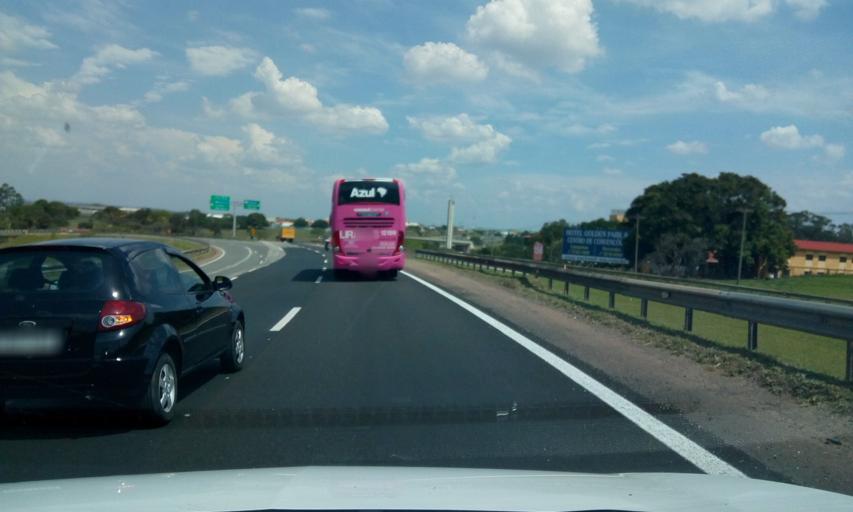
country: BR
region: Sao Paulo
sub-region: Campinas
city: Campinas
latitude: -22.9931
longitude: -47.1106
